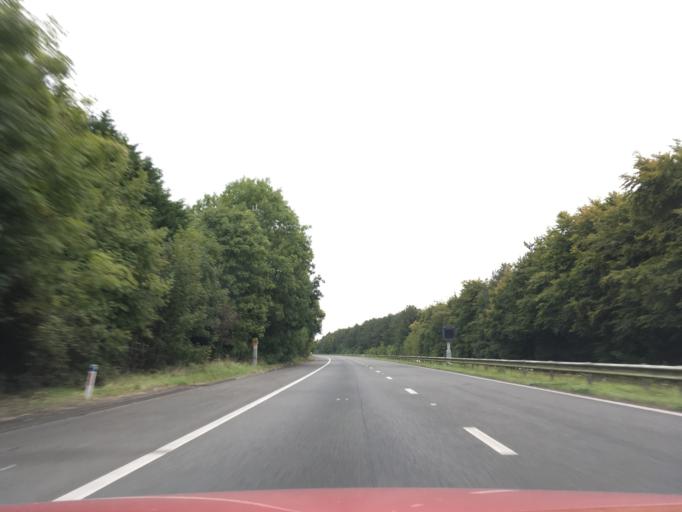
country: GB
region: Wales
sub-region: Monmouthshire
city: Caldicot
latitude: 51.5942
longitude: -2.7650
